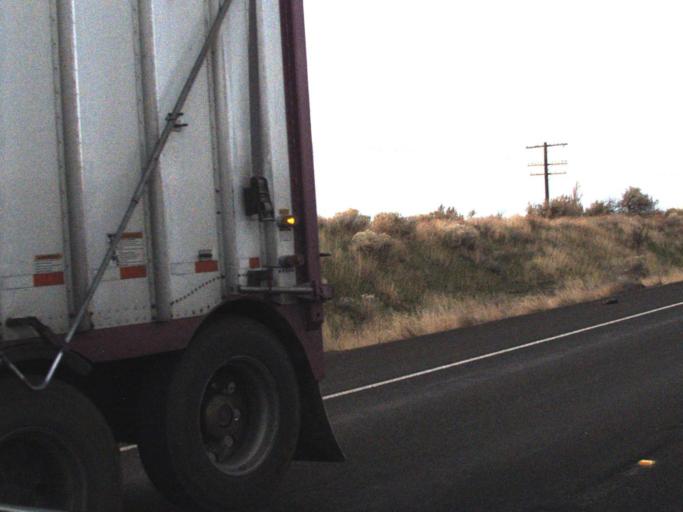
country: US
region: Washington
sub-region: Benton County
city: Finley
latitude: 46.0819
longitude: -118.9086
